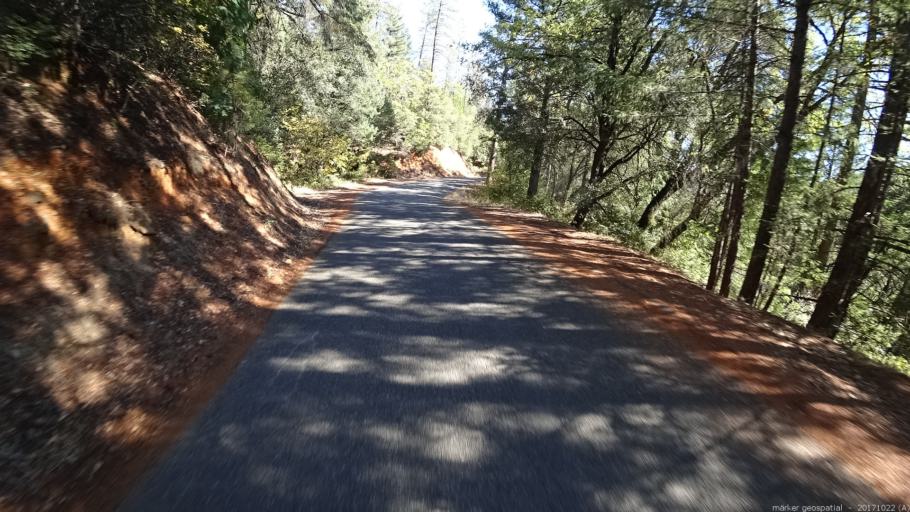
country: US
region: California
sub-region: Shasta County
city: Central Valley (historical)
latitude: 40.9426
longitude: -122.4427
